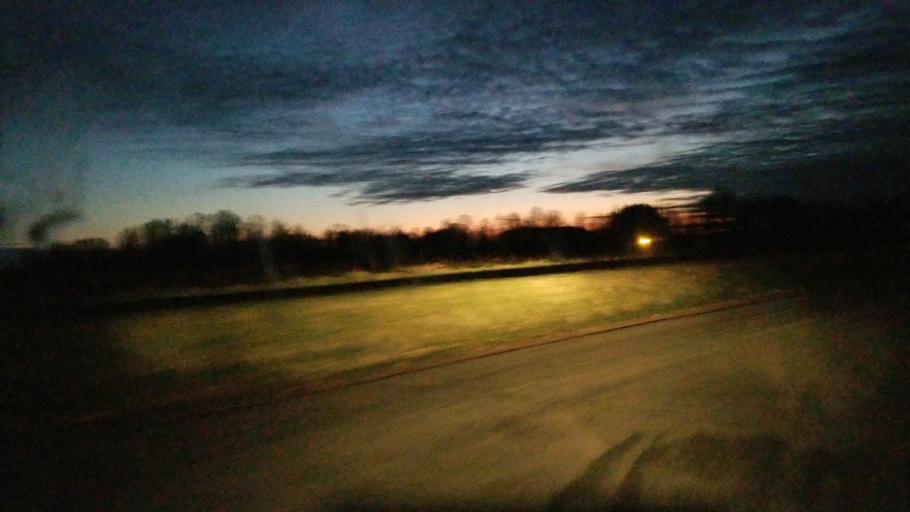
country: US
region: Ohio
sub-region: Muskingum County
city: Dresden
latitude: 40.1009
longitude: -81.8860
